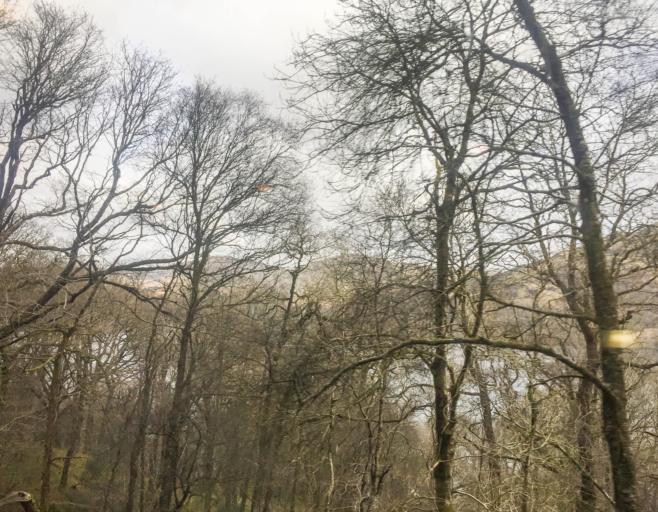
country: GB
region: Scotland
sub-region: Argyll and Bute
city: Garelochhead
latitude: 56.2263
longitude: -4.7000
